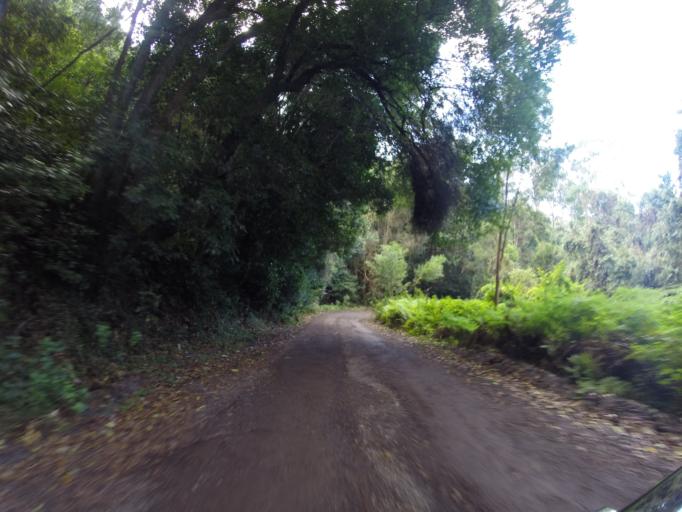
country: AU
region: New South Wales
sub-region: Wollongong
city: Cordeaux Heights
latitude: -34.4365
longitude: 150.7906
